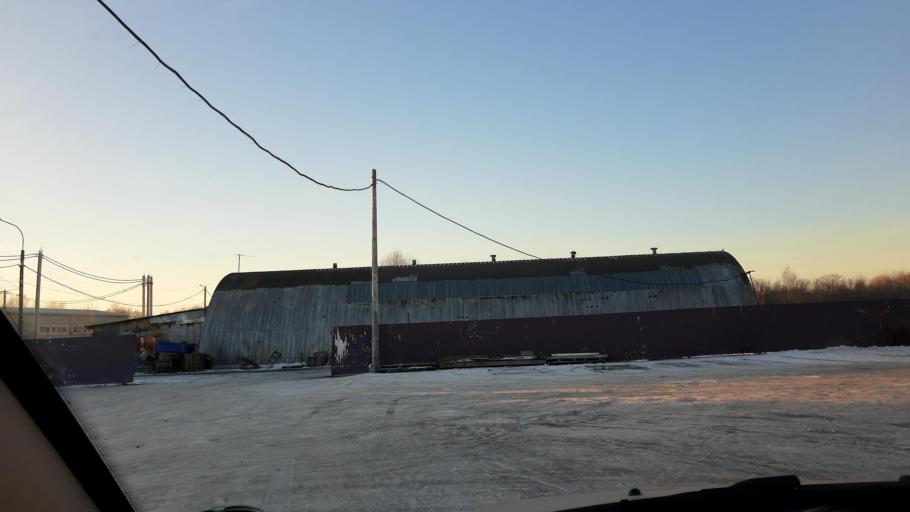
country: RU
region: Nizjnij Novgorod
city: Gorbatovka
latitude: 56.2238
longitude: 43.8102
